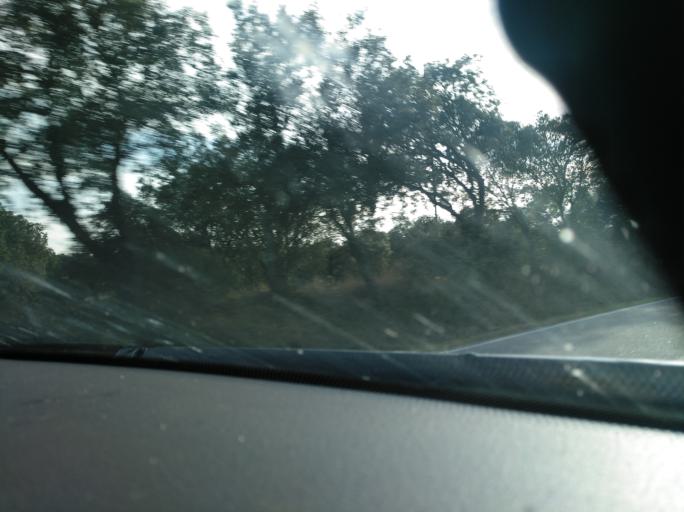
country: PT
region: Portalegre
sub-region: Fronteira
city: Fronteira
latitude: 38.9586
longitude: -7.6345
